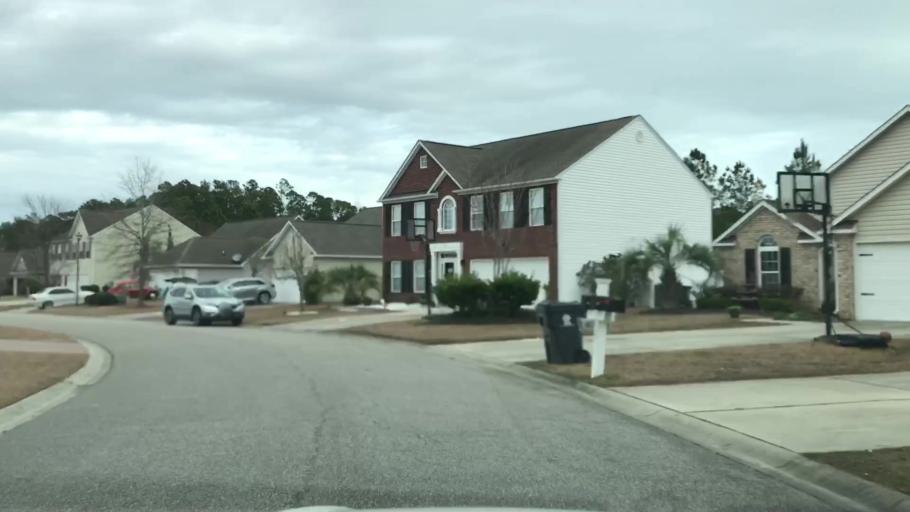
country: US
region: South Carolina
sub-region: Horry County
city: Socastee
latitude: 33.6695
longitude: -78.9728
